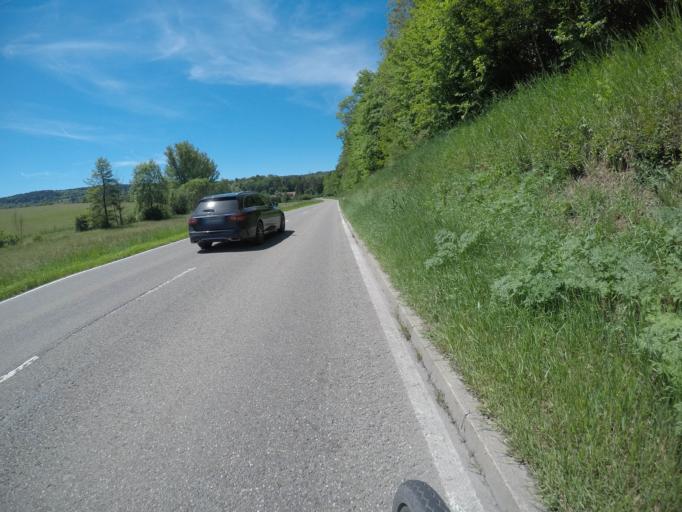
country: DE
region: Baden-Wuerttemberg
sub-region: Karlsruhe Region
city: Heimsheim
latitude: 48.7784
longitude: 8.8403
